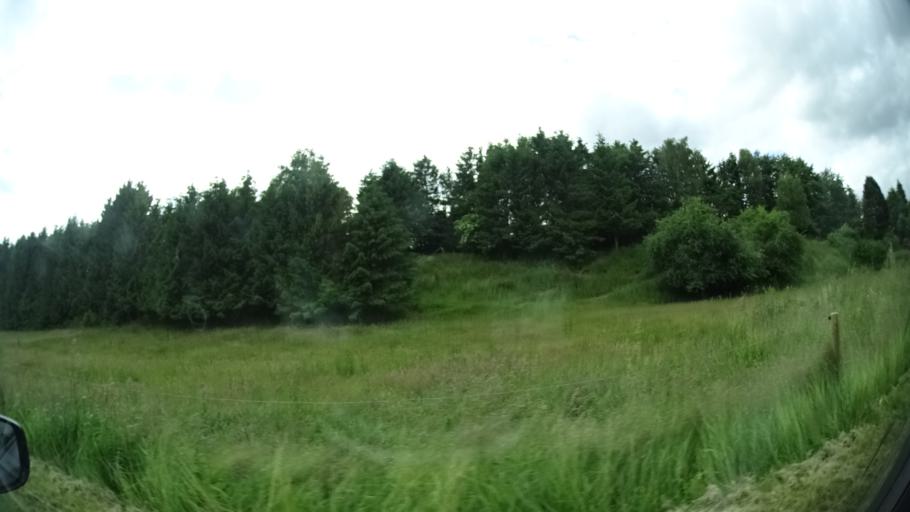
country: DK
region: Central Jutland
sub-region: Syddjurs Kommune
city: Ryomgard
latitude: 56.3859
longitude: 10.5096
